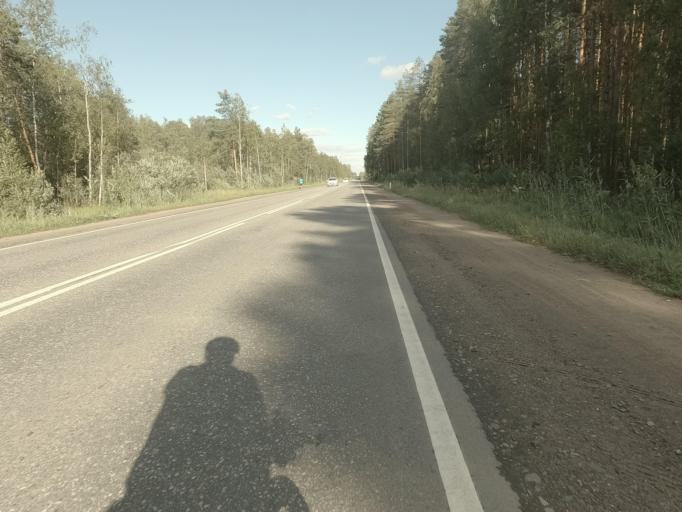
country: RU
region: Leningrad
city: Imeni Morozova
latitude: 59.9748
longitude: 30.9694
